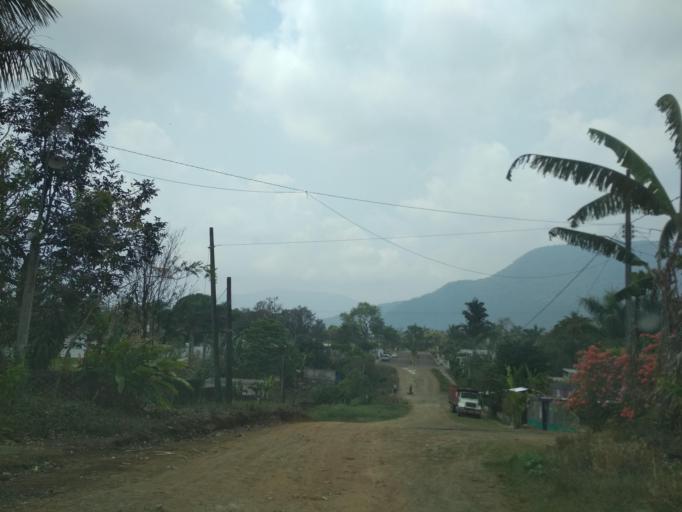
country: MX
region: Veracruz
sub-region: Cordoba
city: San Jose de Tapia
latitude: 18.8505
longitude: -96.9798
